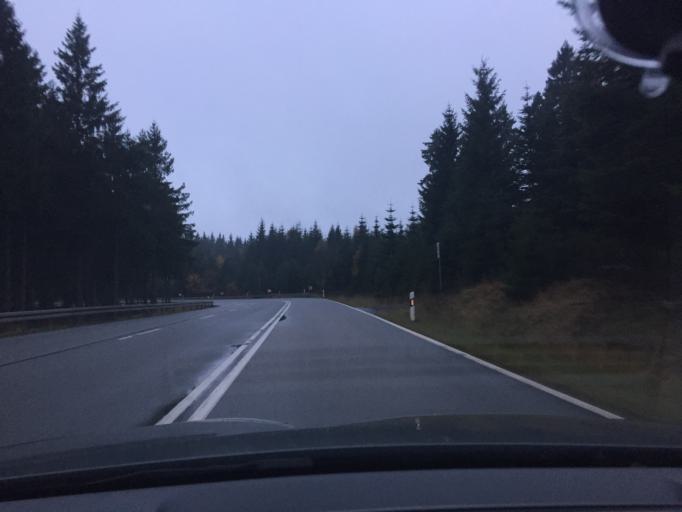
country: DE
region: Saxony
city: Altenberg
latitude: 50.7726
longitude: 13.7237
